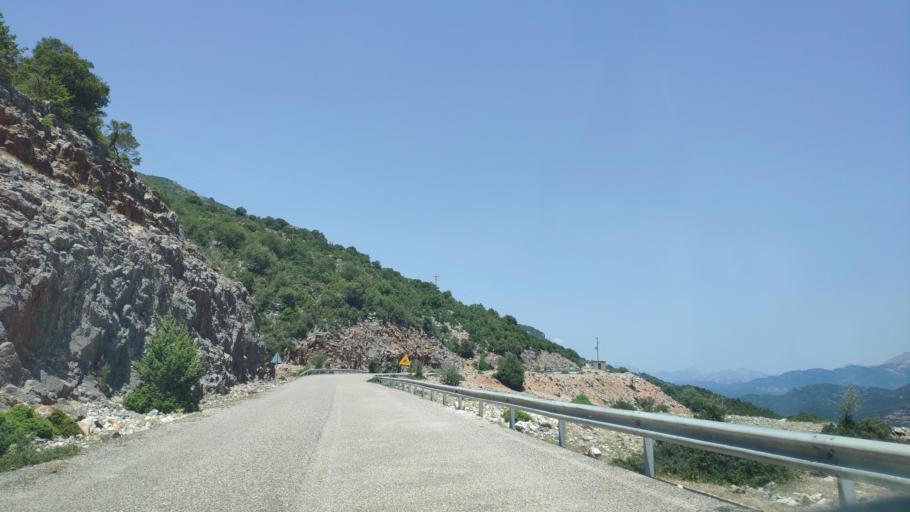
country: GR
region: Thessaly
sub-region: Nomos Kardhitsas
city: Anthiro
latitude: 39.1268
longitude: 21.3977
